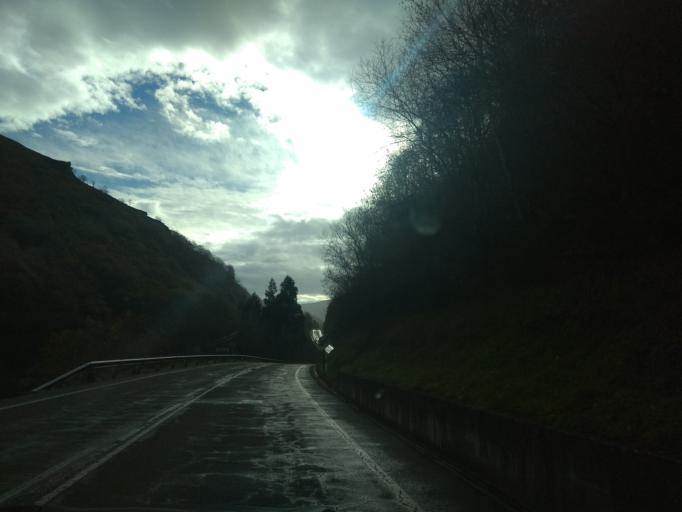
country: ES
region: Cantabria
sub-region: Provincia de Cantabria
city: San Pedro del Romeral
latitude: 43.1368
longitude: -3.9003
